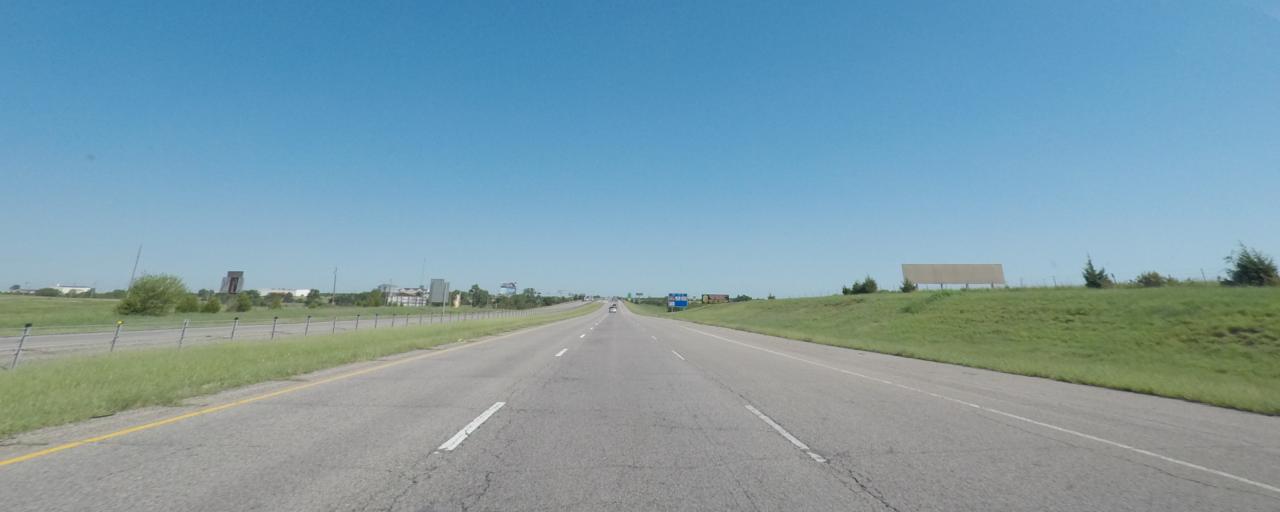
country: US
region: Oklahoma
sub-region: Noble County
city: Perry
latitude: 36.2789
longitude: -97.3276
